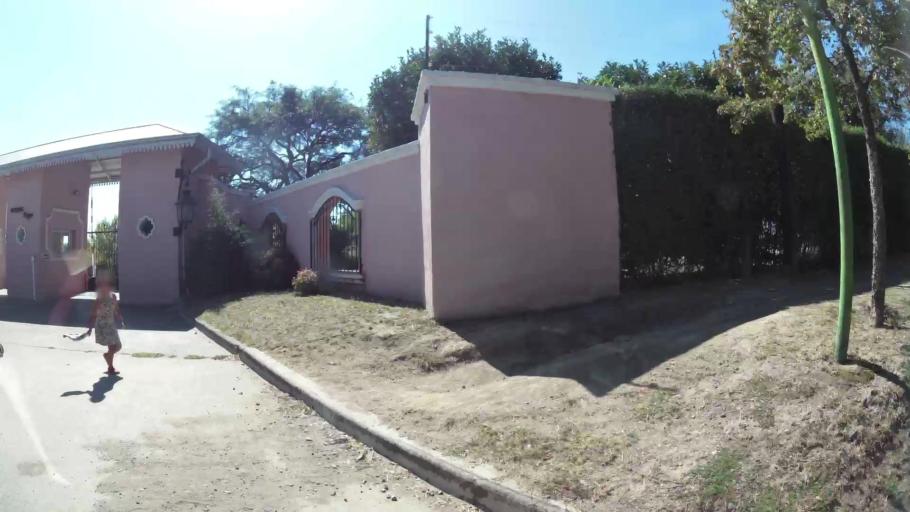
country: AR
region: Cordoba
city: Villa Allende
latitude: -31.2978
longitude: -64.2793
